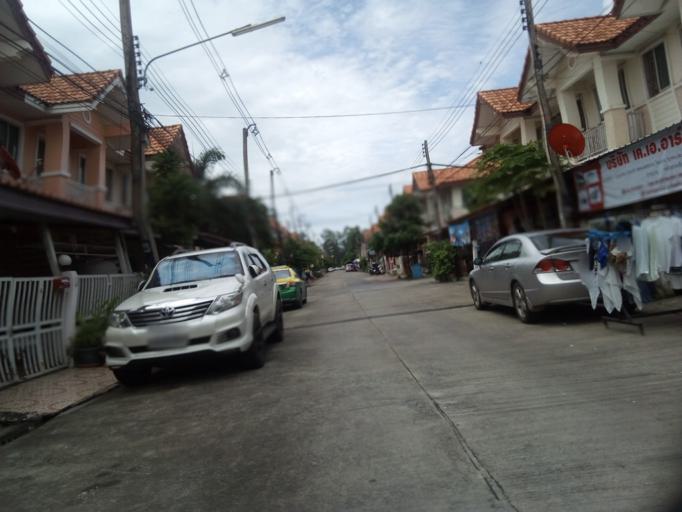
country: TH
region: Pathum Thani
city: Ban Rangsit
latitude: 14.0465
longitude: 100.8345
